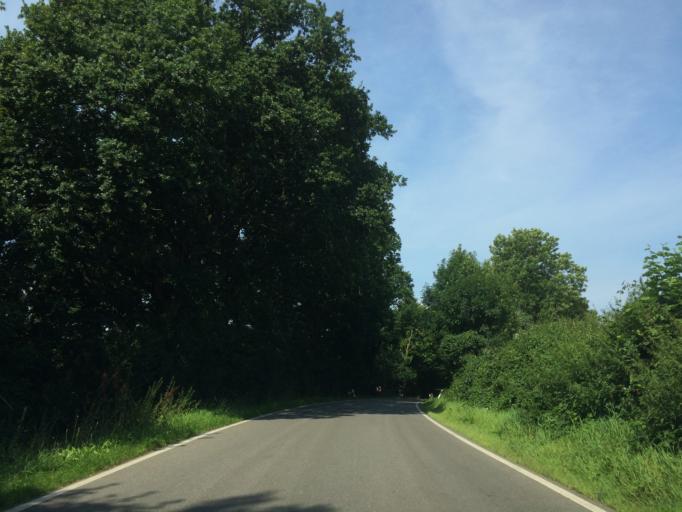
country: DE
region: Schleswig-Holstein
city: Altenhof
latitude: 54.4210
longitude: 9.8908
